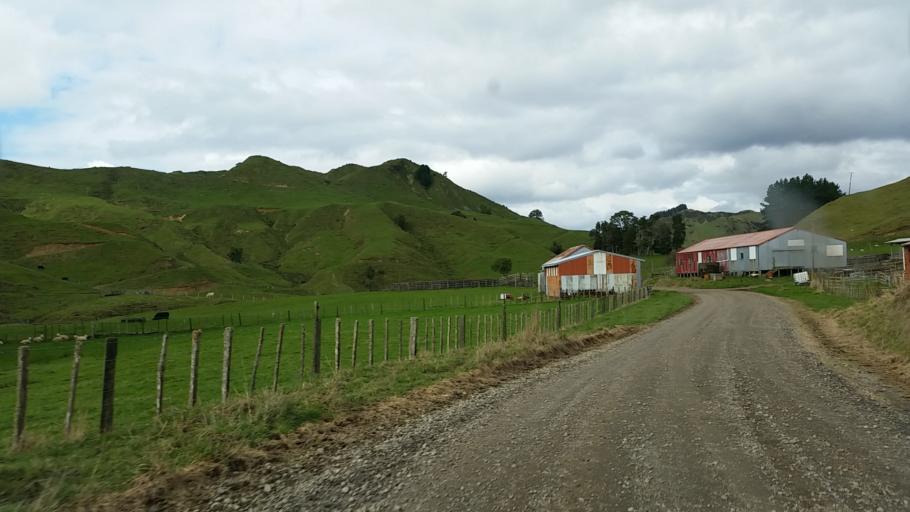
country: NZ
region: Taranaki
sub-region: New Plymouth District
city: Waitara
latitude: -39.1605
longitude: 174.5940
